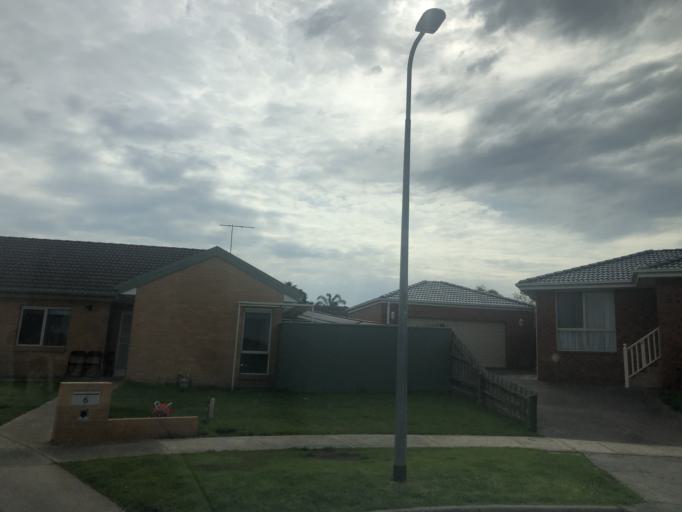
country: AU
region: Victoria
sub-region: Casey
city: Hallam
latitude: -38.0133
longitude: 145.2817
